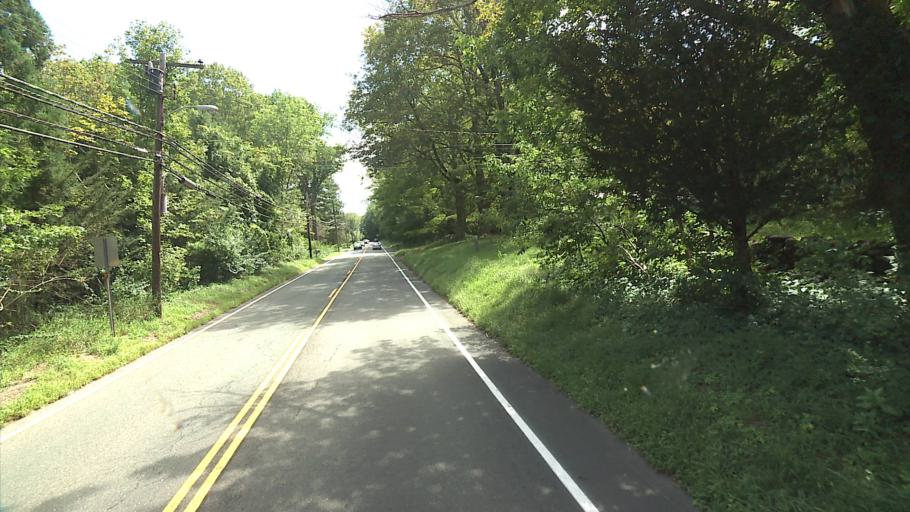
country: US
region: Connecticut
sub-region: Tolland County
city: Storrs
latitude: 41.8256
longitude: -72.2646
